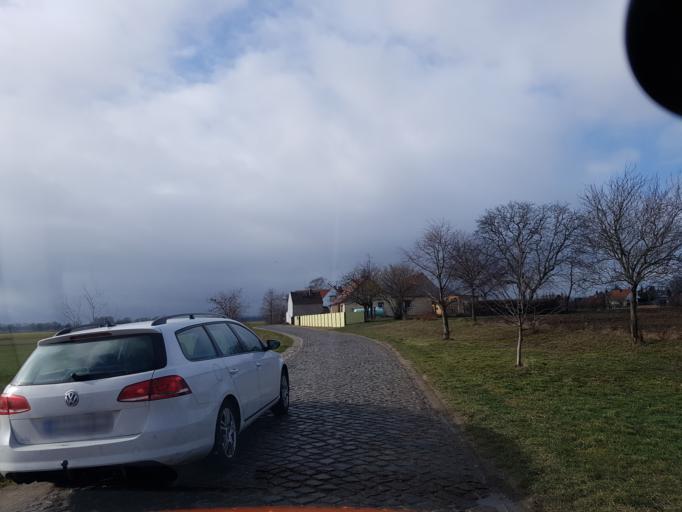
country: DE
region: Brandenburg
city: Muhlberg
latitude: 51.4773
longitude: 13.2014
